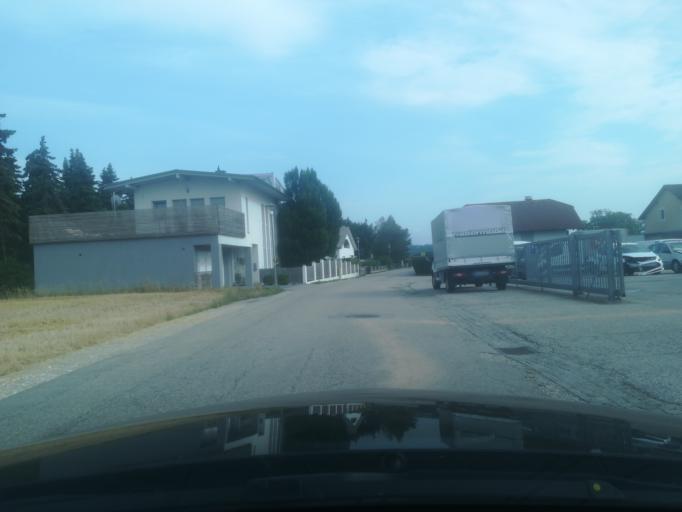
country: AT
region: Upper Austria
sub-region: Wels-Land
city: Marchtrenk
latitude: 48.1934
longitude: 14.1292
